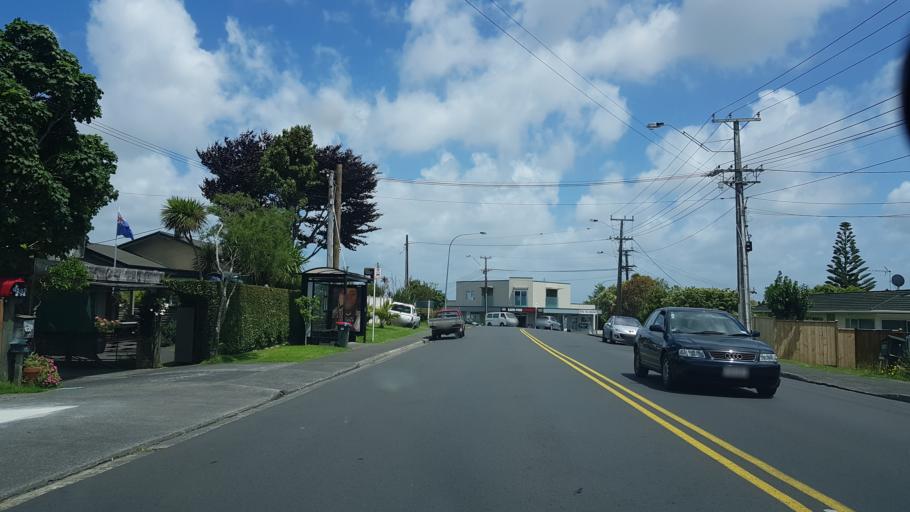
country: NZ
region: Auckland
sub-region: Auckland
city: North Shore
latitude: -36.8090
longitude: 174.7006
